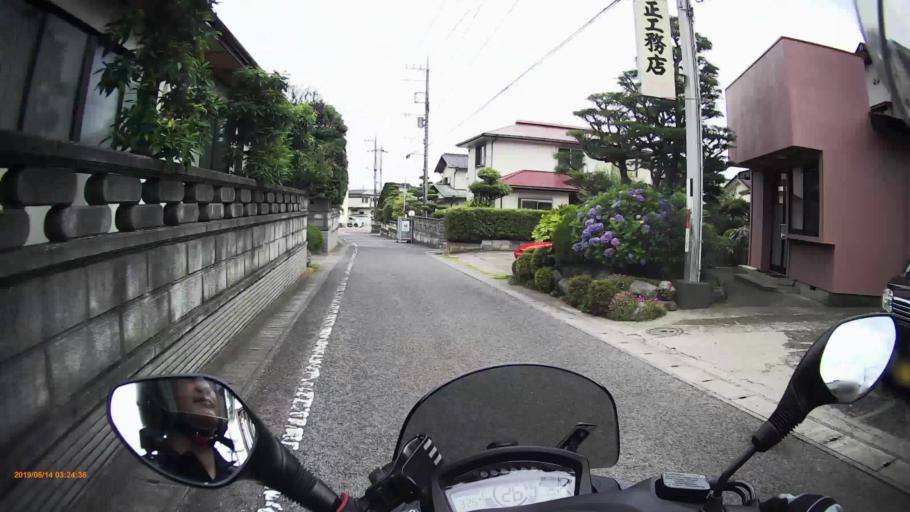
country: JP
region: Kanagawa
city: Minami-rinkan
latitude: 35.4144
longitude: 139.4506
